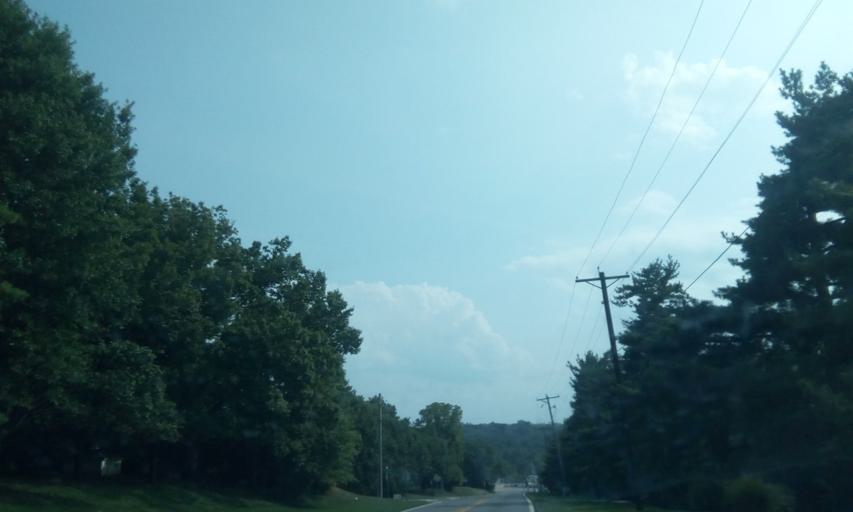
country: US
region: Missouri
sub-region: Saint Louis County
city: Town and Country
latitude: 38.5988
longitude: -90.4795
